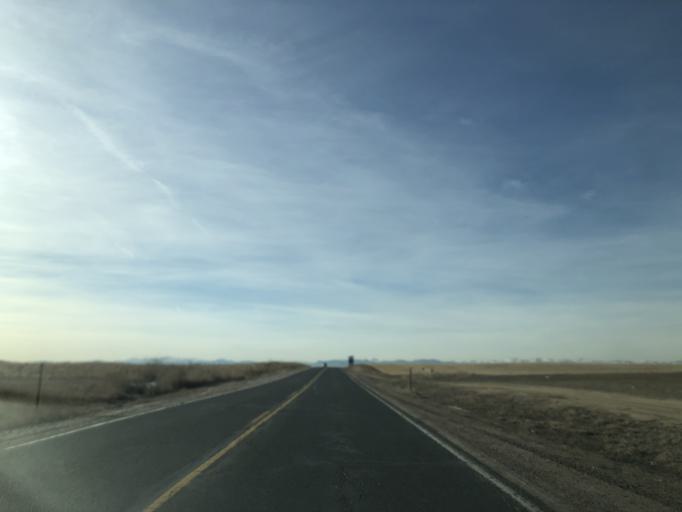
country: US
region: Colorado
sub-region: Adams County
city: Aurora
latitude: 39.7984
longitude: -104.7240
